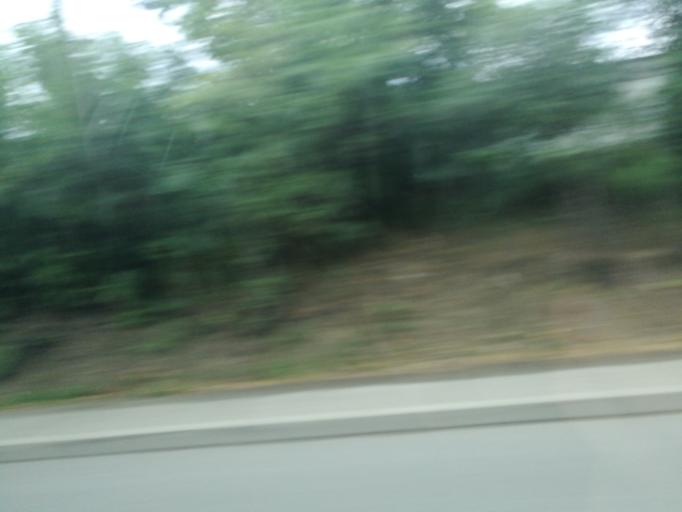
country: RO
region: Mures
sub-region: Comuna Sangeorgiu de Mures
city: Sangeorgiu de Mures
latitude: 46.5749
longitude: 24.6022
